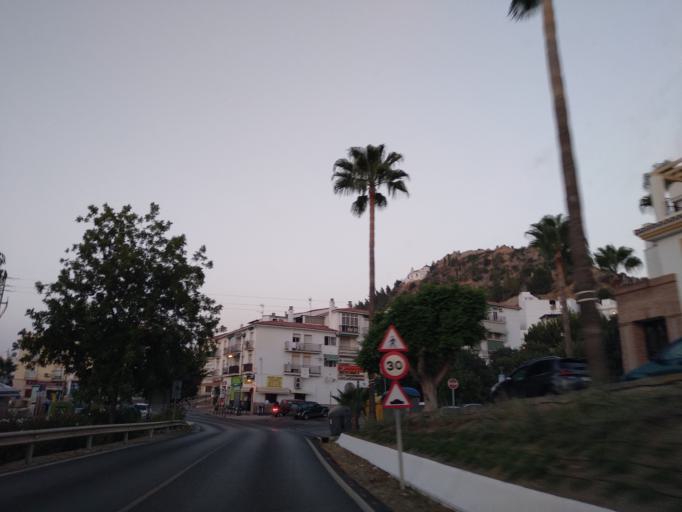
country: ES
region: Andalusia
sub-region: Provincia de Malaga
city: Cartama
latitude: 36.7091
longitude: -4.6346
